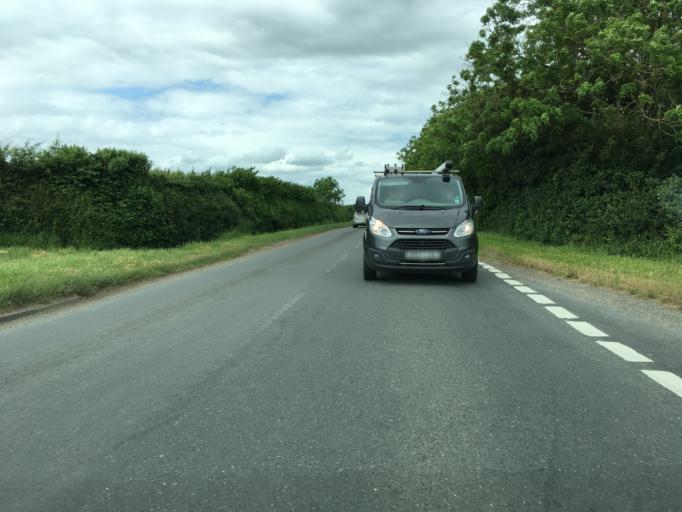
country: GB
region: England
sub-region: Gloucestershire
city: Cirencester
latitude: 51.6770
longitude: -1.9688
